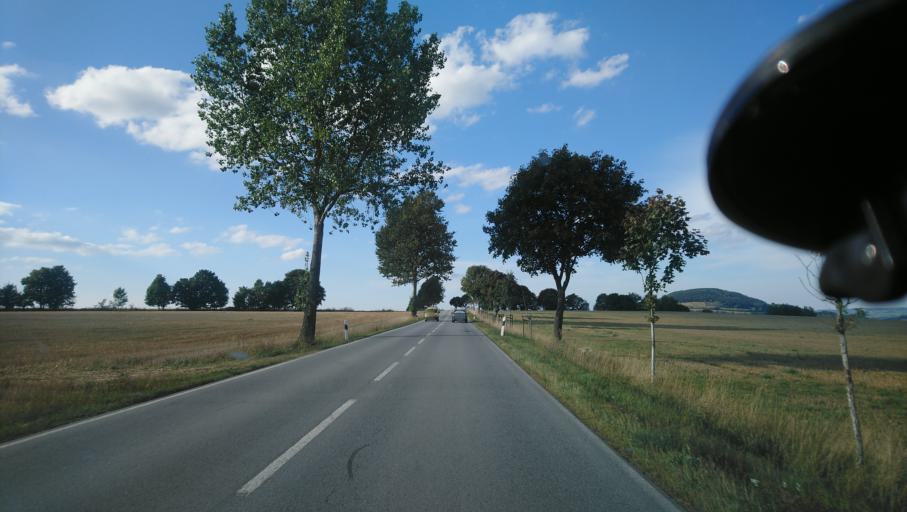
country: DE
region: Saxony
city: Konigswalde
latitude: 50.5386
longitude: 13.0232
